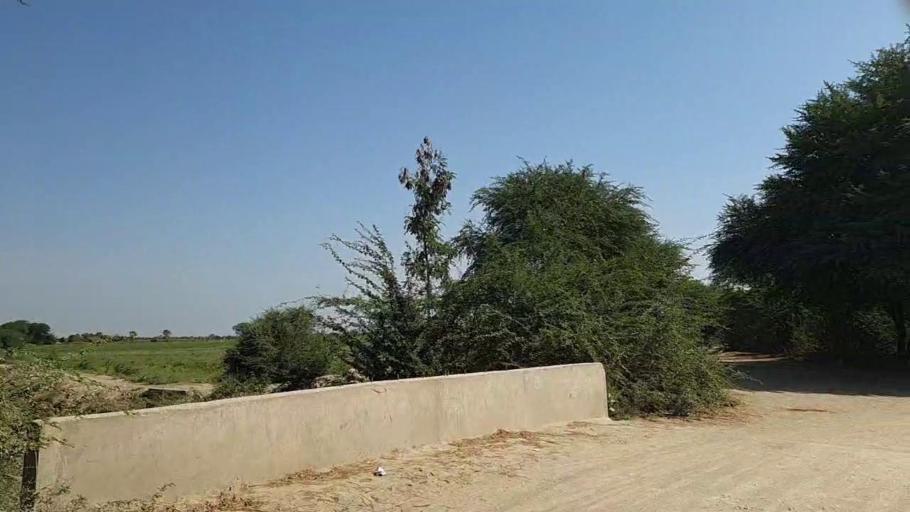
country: PK
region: Sindh
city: Mirpur Batoro
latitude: 24.6861
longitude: 68.2811
